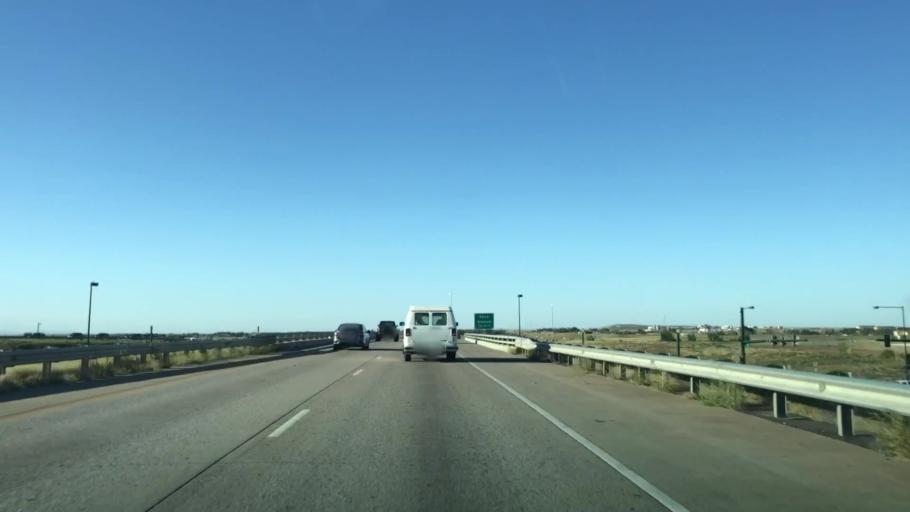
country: US
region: Colorado
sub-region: Adams County
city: Aurora
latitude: 39.7830
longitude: -104.7905
